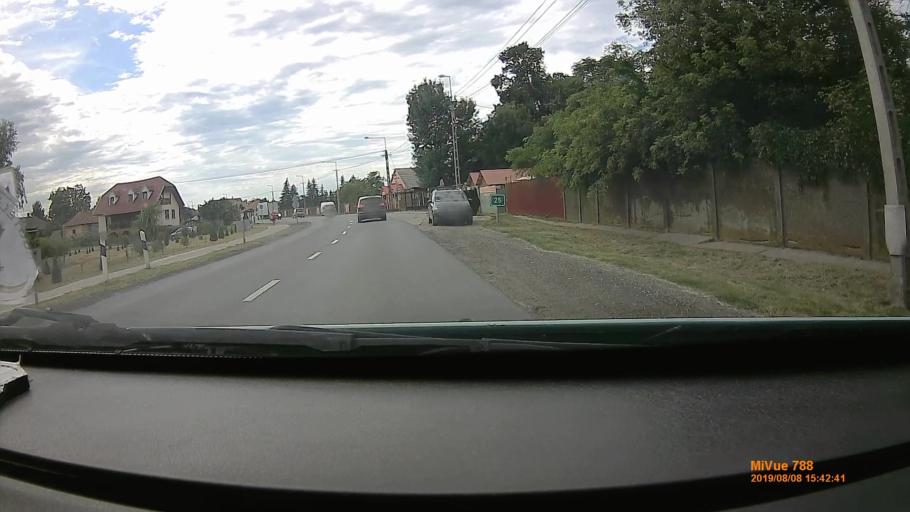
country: HU
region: Szabolcs-Szatmar-Bereg
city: Kocsord
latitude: 47.9389
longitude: 22.3967
